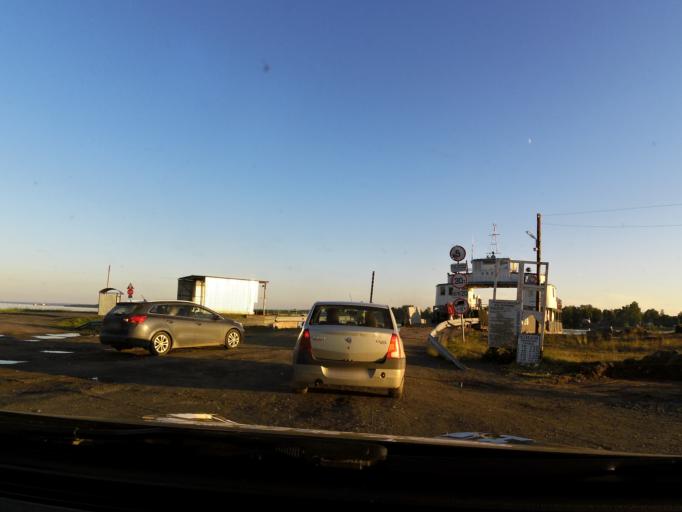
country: RU
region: Leningrad
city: Voznesen'ye
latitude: 61.0154
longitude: 35.4930
